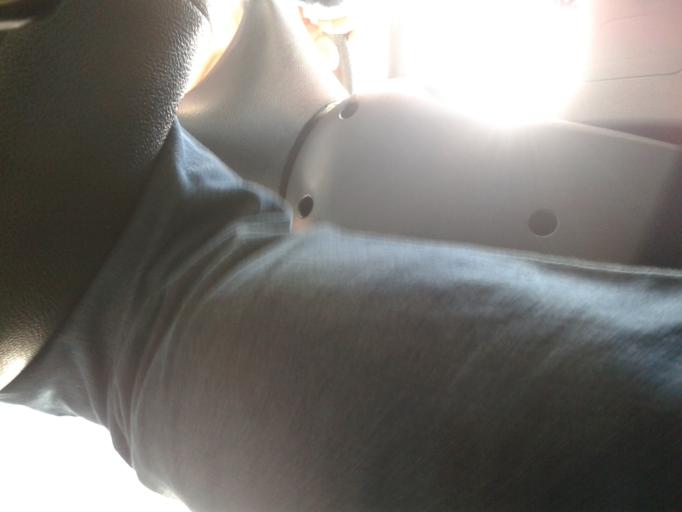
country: BR
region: Minas Gerais
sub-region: Ituiutaba
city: Ituiutaba
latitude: -19.0768
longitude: -49.7574
